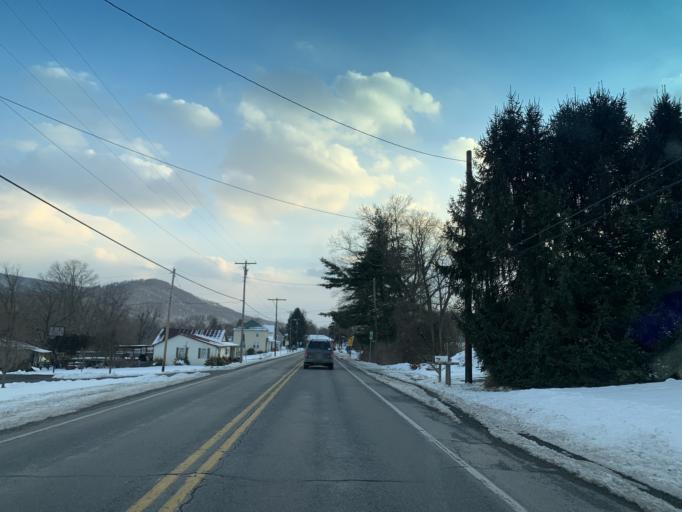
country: US
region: Maryland
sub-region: Allegany County
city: Cumberland
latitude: 39.7252
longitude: -78.7739
